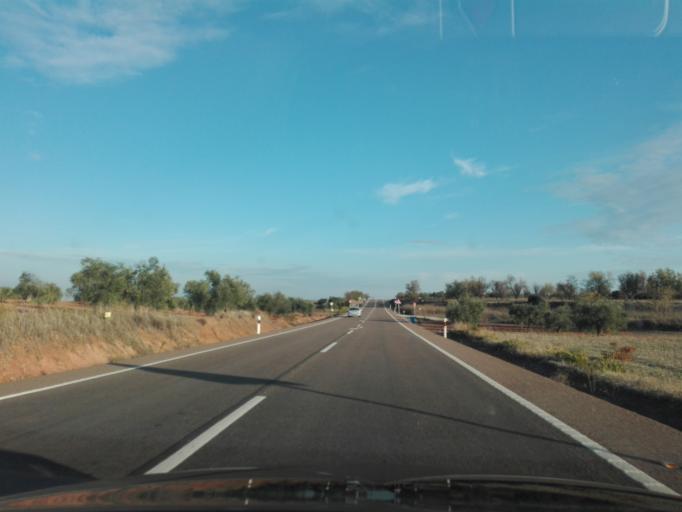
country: ES
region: Extremadura
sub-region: Provincia de Badajoz
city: Usagre
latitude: 38.3527
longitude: -6.1980
